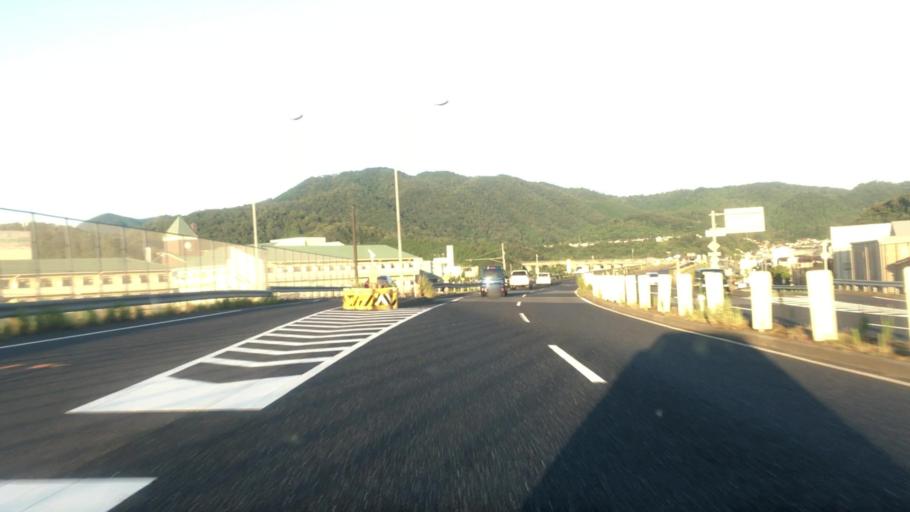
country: JP
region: Tottori
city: Tottori
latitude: 35.5240
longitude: 134.2251
